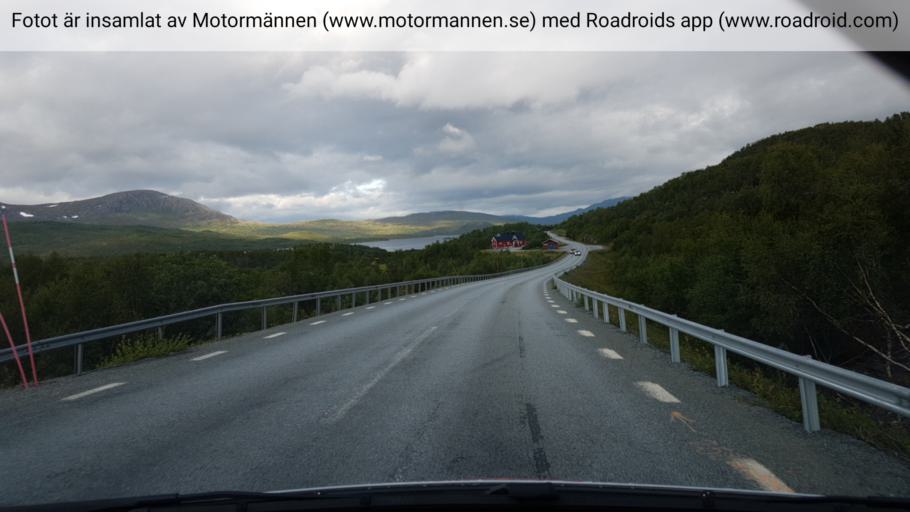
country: NO
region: Nordland
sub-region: Rana
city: Mo i Rana
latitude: 66.0513
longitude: 14.8875
